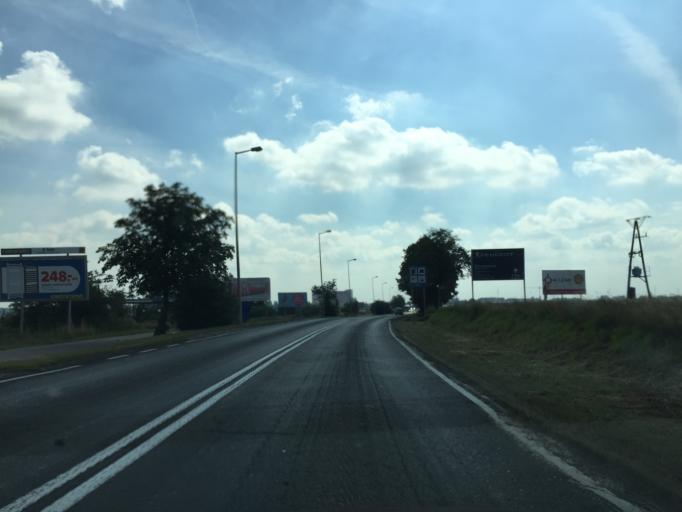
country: PL
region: Greater Poland Voivodeship
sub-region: Kalisz
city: Kalisz
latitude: 51.7682
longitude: 18.0491
